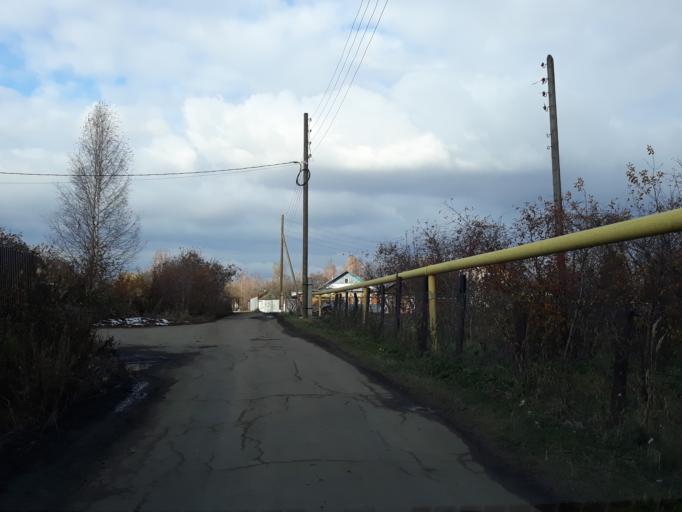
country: RU
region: Nizjnij Novgorod
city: Afonino
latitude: 56.2326
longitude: 44.0147
